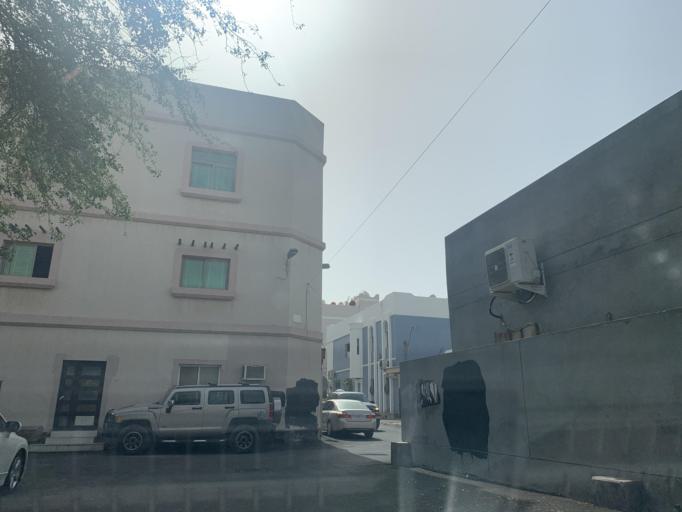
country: BH
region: Northern
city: Madinat `Isa
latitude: 26.1571
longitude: 50.5178
